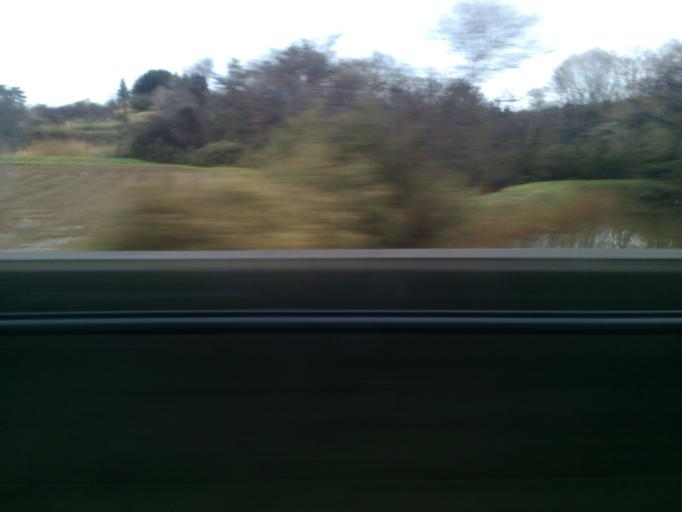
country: JP
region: Miyagi
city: Kogota
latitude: 38.6781
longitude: 141.0317
